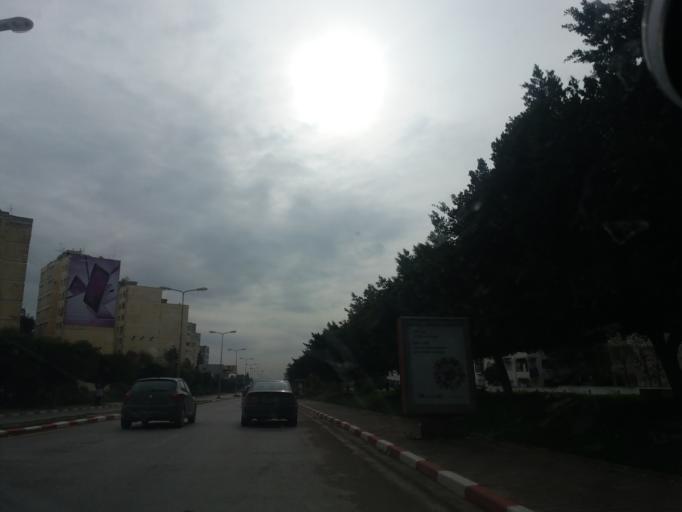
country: TN
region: Tunis
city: Tunis
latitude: 36.8456
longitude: 10.1620
